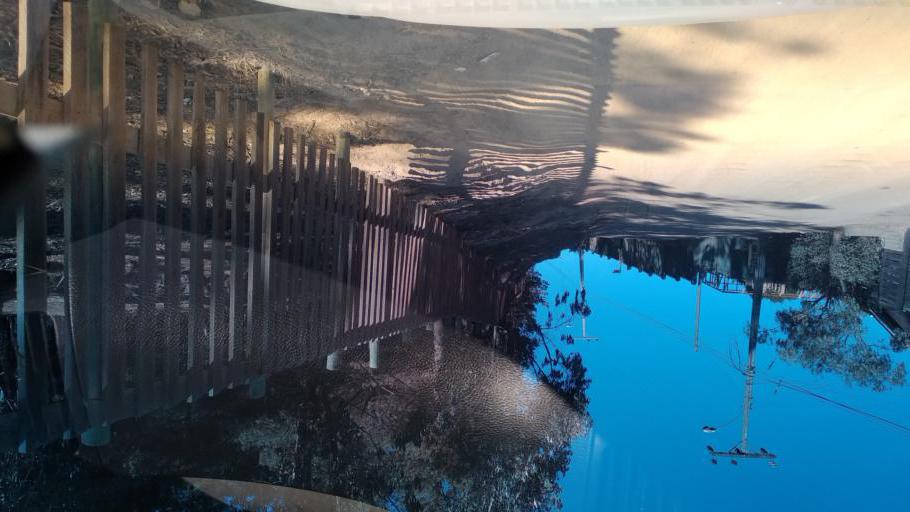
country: CL
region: O'Higgins
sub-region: Provincia de Colchagua
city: Santa Cruz
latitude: -34.3939
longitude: -72.0112
